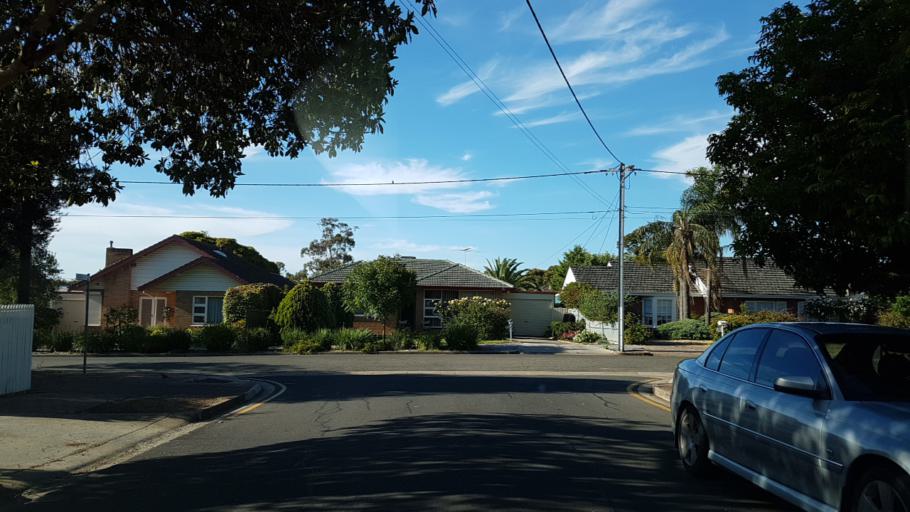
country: AU
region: South Australia
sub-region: Campbelltown
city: Campbelltown
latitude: -34.8933
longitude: 138.6781
